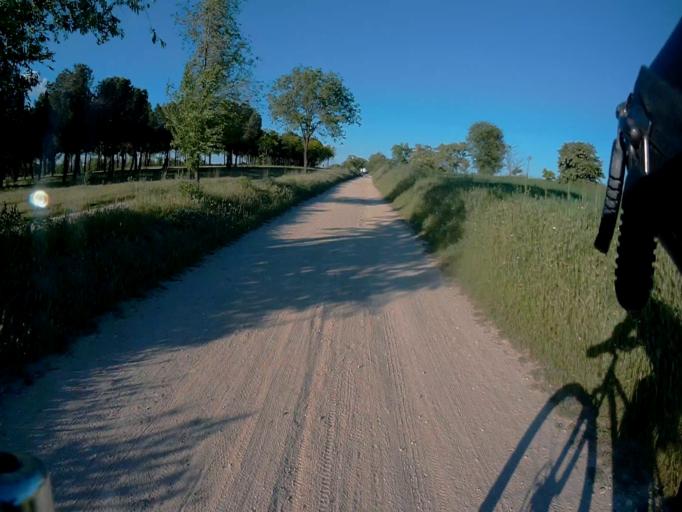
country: ES
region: Madrid
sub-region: Provincia de Madrid
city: Fuenlabrada
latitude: 40.3136
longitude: -3.8015
